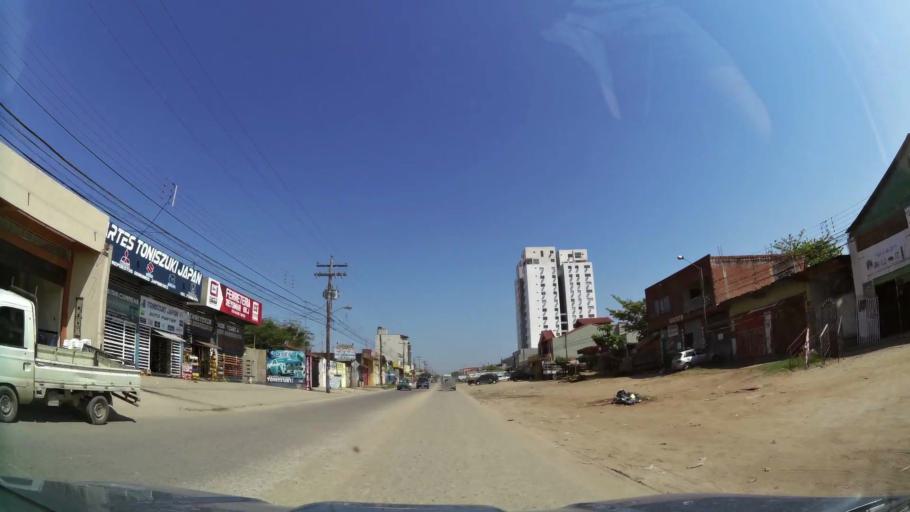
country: BO
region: Santa Cruz
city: Santa Cruz de la Sierra
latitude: -17.7381
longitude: -63.1461
